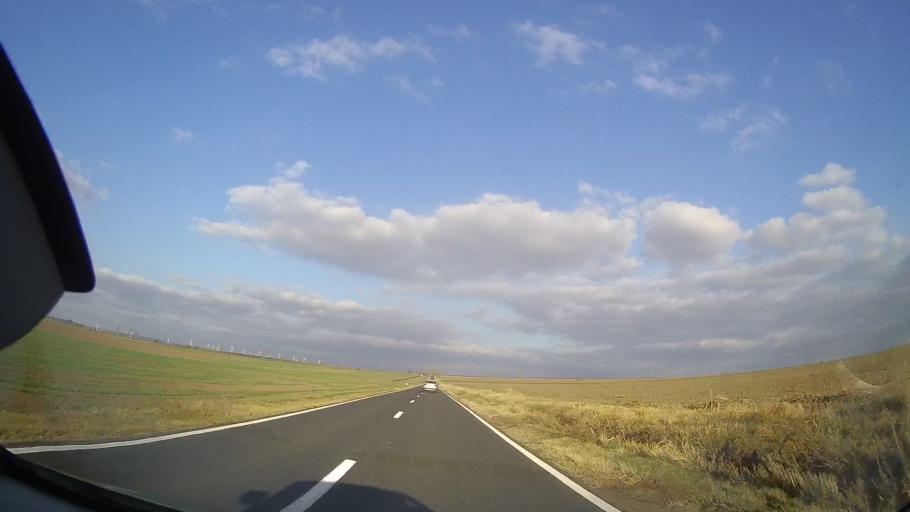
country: RO
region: Tulcea
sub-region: Comuna Topolog
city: Topolog
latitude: 44.8421
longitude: 28.3074
